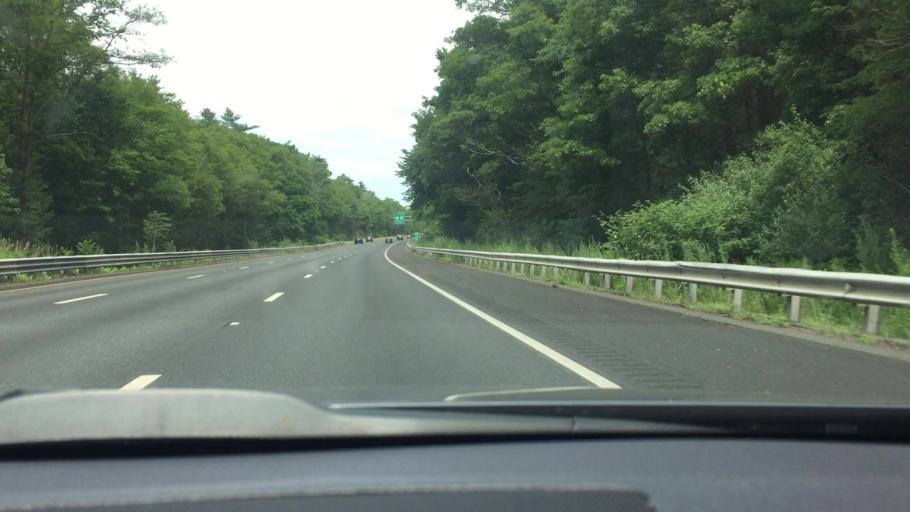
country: US
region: Massachusetts
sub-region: Norfolk County
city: Walpole
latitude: 42.1113
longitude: -71.2311
